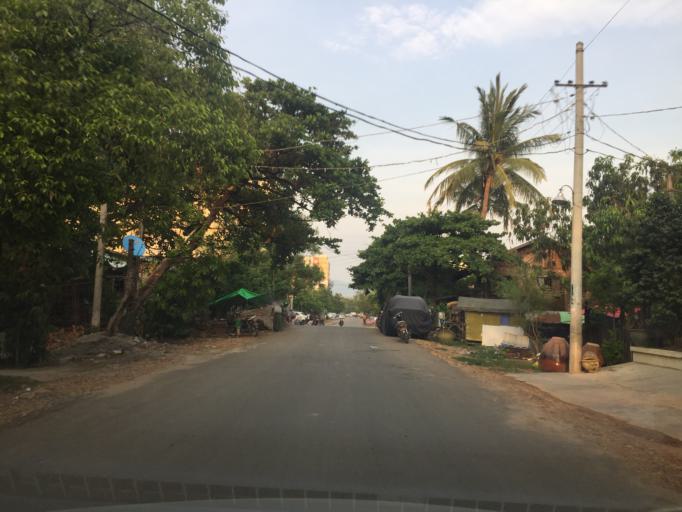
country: MM
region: Mandalay
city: Mandalay
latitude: 21.9716
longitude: 96.0984
